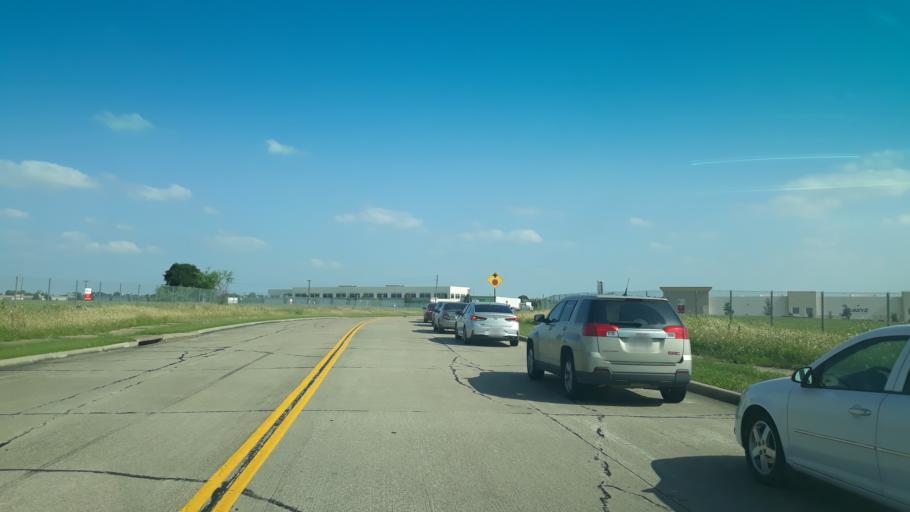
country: US
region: Texas
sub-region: Tarrant County
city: Euless
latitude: 32.8683
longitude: -97.0083
